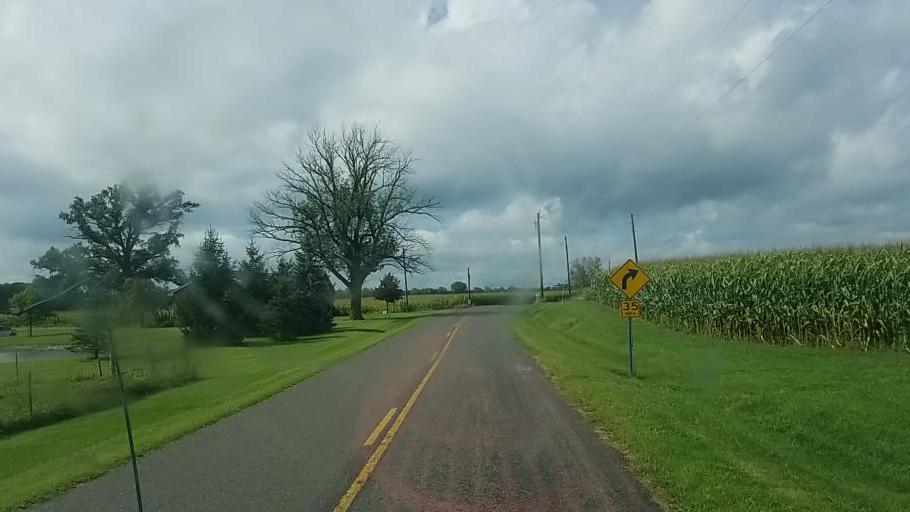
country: US
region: Ohio
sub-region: Hardin County
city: Kenton
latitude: 40.4920
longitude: -83.5182
